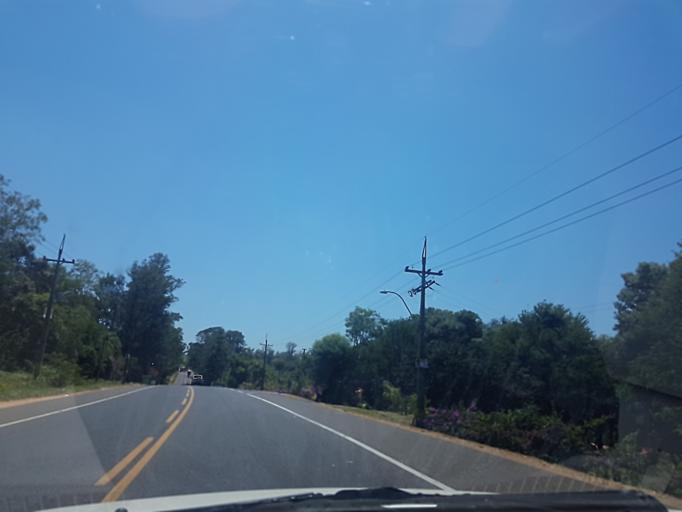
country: PY
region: Cordillera
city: Caacupe
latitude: -25.3908
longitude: -57.0699
